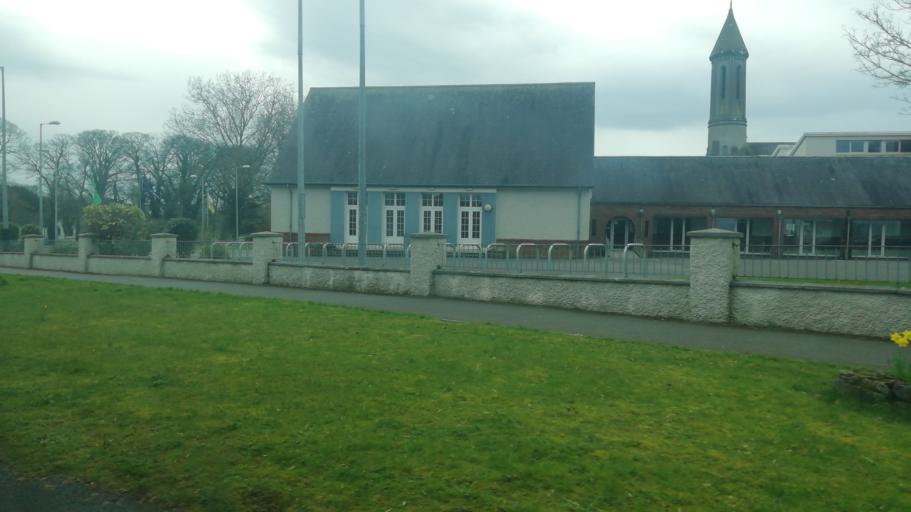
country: IE
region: Leinster
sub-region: Kildare
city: Rathangan
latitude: 53.2231
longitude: -6.9883
